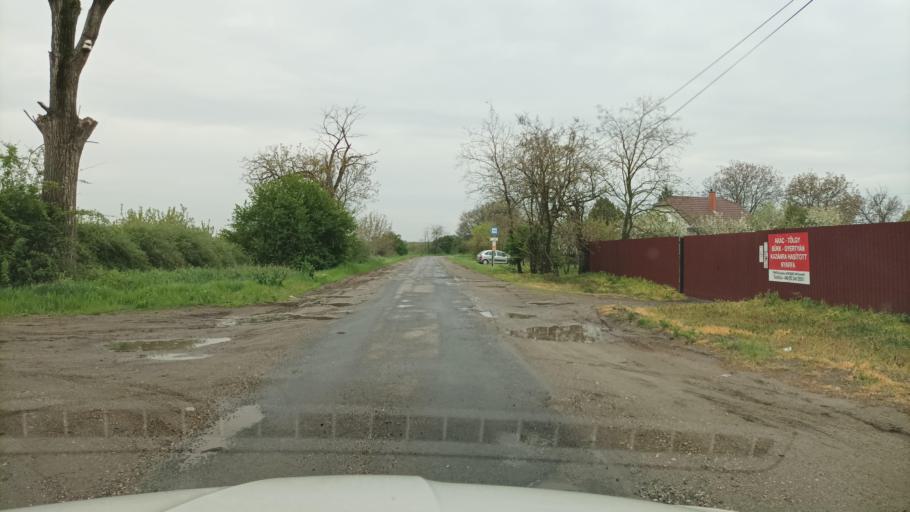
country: HU
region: Pest
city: Nagykoros
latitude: 47.0186
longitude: 19.7920
